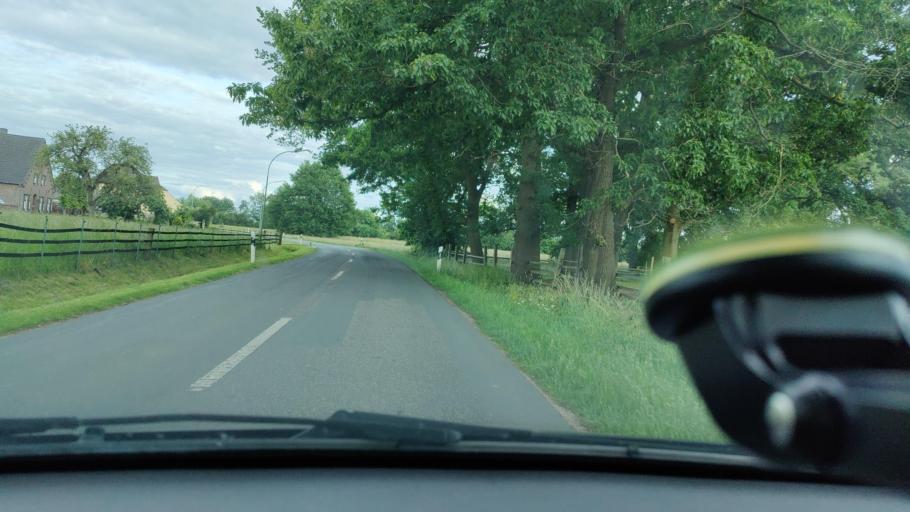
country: DE
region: North Rhine-Westphalia
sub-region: Regierungsbezirk Dusseldorf
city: Goch
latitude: 51.6421
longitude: 6.1278
